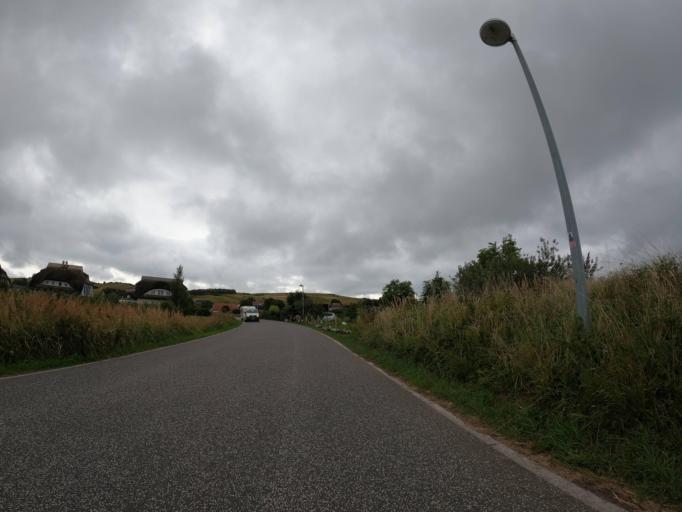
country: DE
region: Mecklenburg-Vorpommern
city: Ostseebad Gohren
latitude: 54.3104
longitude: 13.6808
